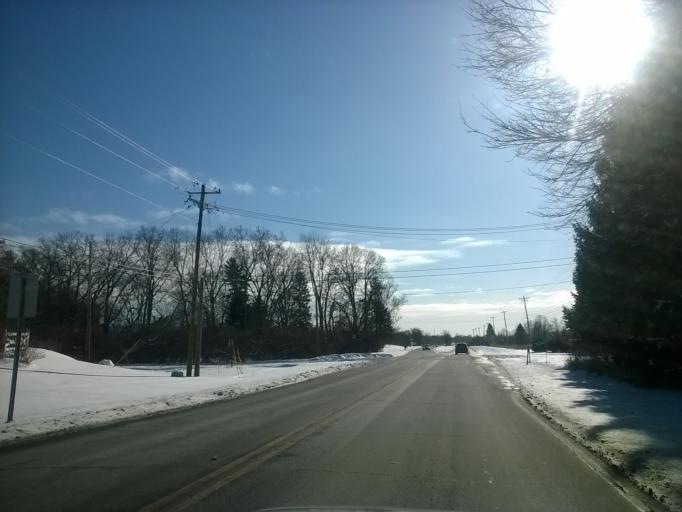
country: US
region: Indiana
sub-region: Hamilton County
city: Carmel
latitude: 39.9349
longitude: -86.1269
